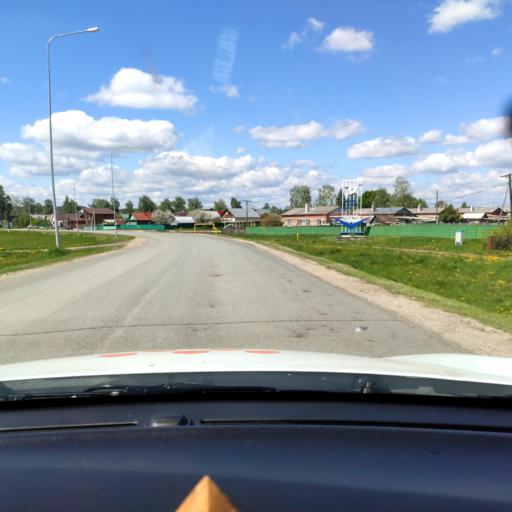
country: RU
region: Tatarstan
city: Kuybyshevskiy Zaton
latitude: 55.1603
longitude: 49.1828
